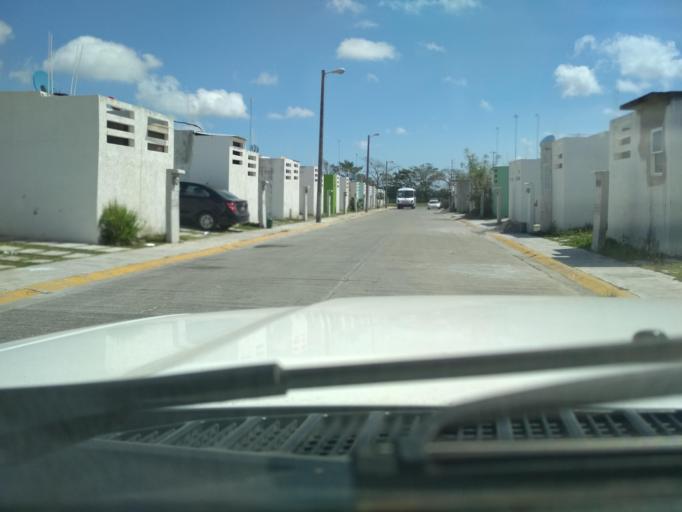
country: MX
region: Veracruz
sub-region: Veracruz
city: Las Amapolas
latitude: 19.1383
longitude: -96.2218
